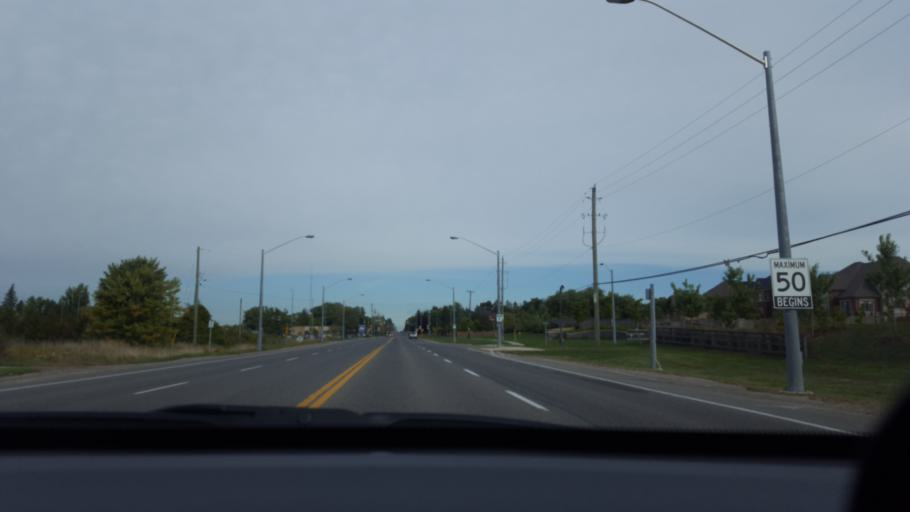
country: CA
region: Ontario
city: Vaughan
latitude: 43.9181
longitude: -79.5254
